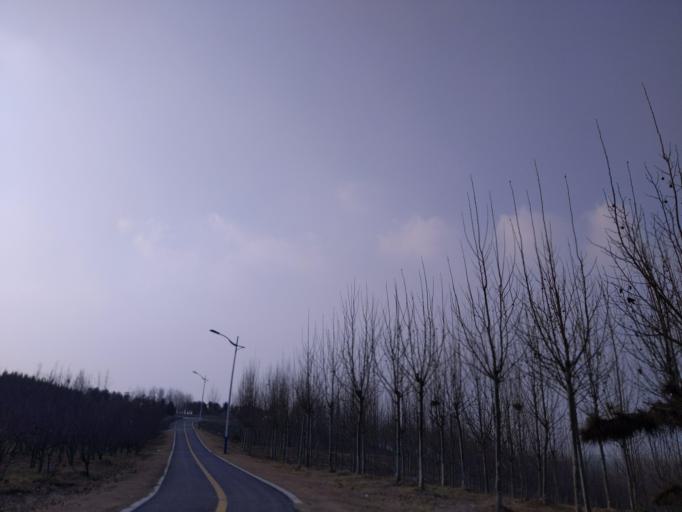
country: CN
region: Henan Sheng
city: Puyang
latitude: 35.8198
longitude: 115.0214
